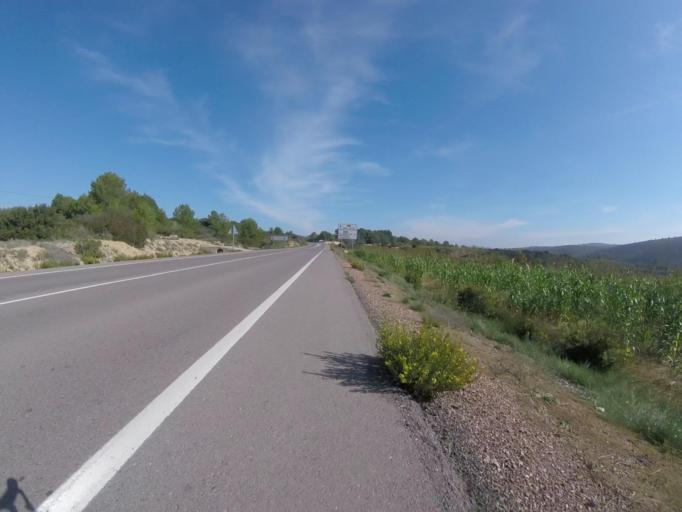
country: ES
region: Valencia
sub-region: Provincia de Castello
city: Benlloch
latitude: 40.2561
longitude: 0.0767
